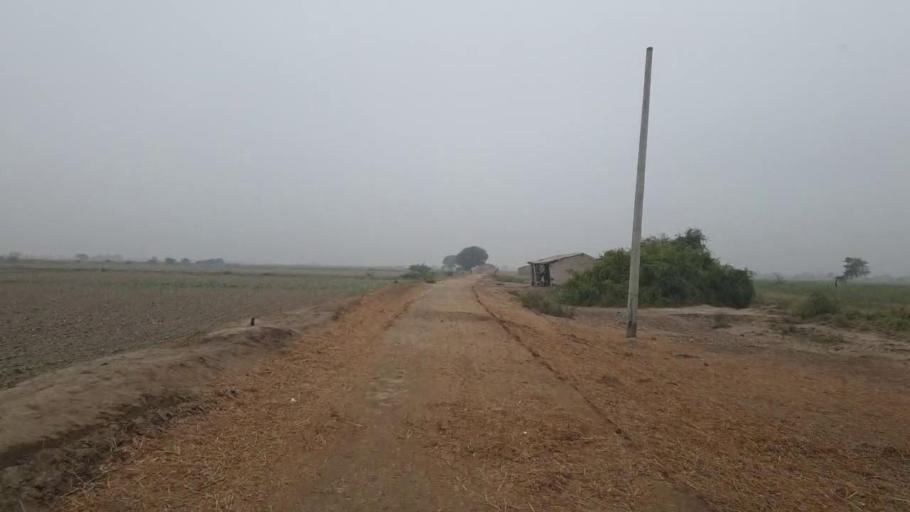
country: PK
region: Sindh
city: Badin
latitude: 24.6321
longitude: 68.6781
